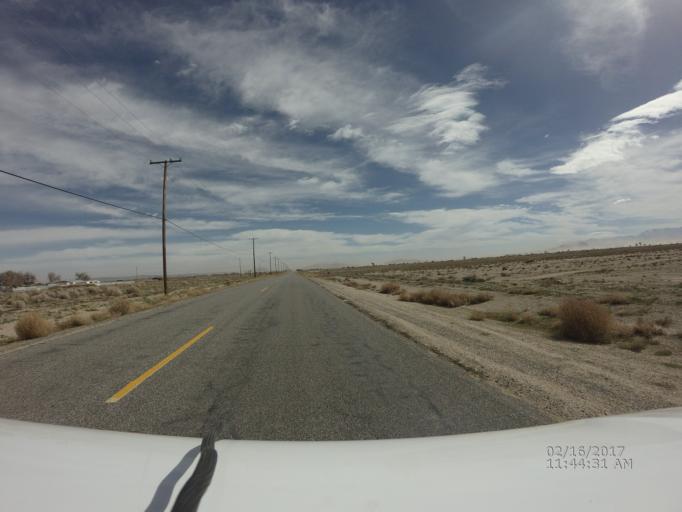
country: US
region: California
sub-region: Los Angeles County
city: Lake Los Angeles
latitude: 34.6901
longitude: -117.9495
